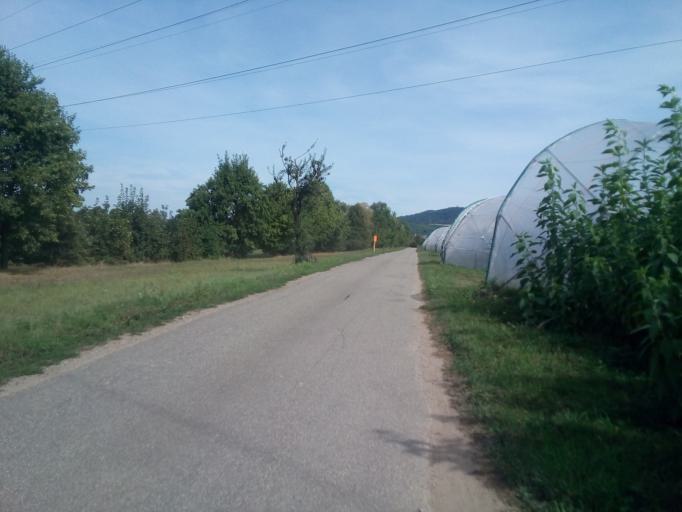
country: DE
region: Baden-Wuerttemberg
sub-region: Karlsruhe Region
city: Ottenhofen
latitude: 48.7518
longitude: 8.1431
